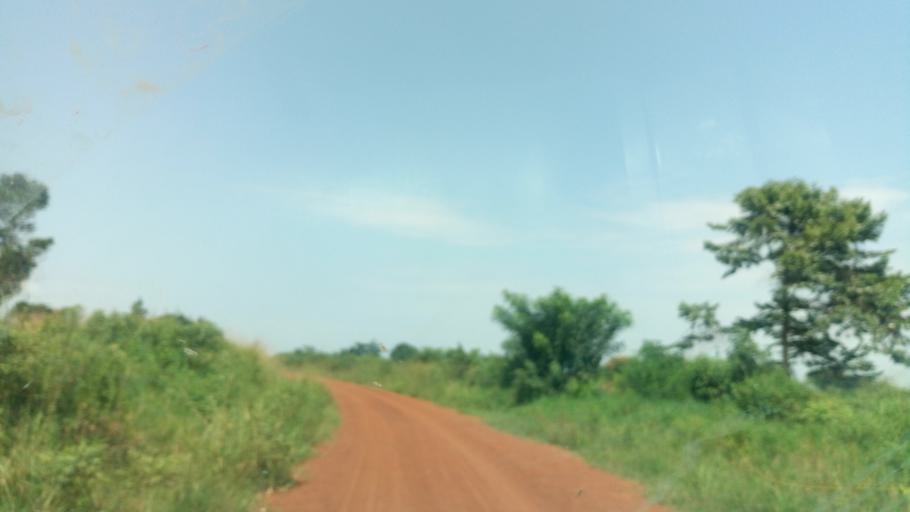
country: UG
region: Western Region
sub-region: Masindi District
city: Masindi
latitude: 1.6834
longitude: 31.8326
